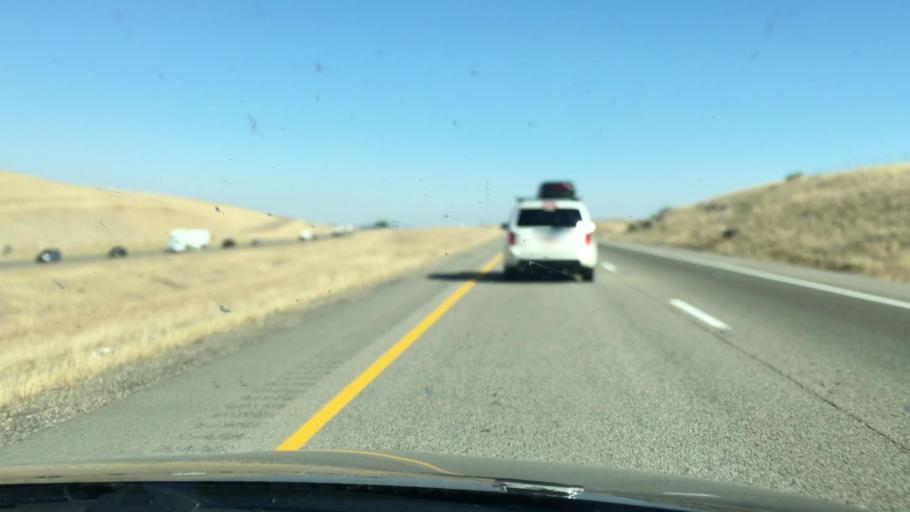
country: US
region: Idaho
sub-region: Ada County
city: Boise
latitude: 43.4888
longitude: -116.1233
